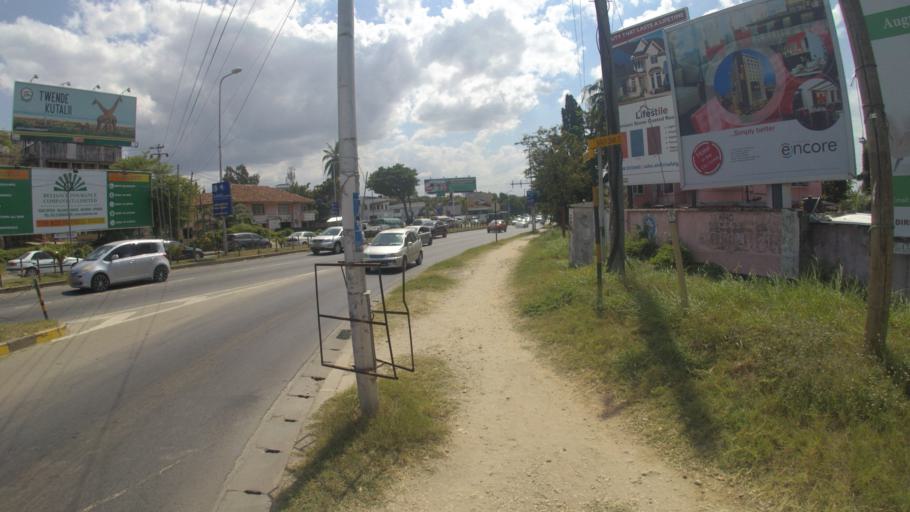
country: TZ
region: Dar es Salaam
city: Dar es Salaam
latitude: -6.7983
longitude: 39.2825
